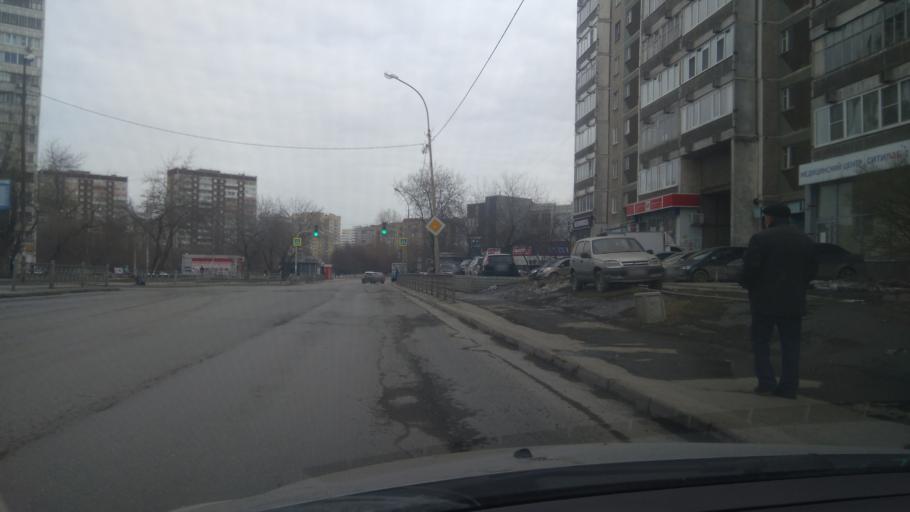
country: RU
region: Sverdlovsk
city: Yekaterinburg
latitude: 56.8543
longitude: 60.5593
